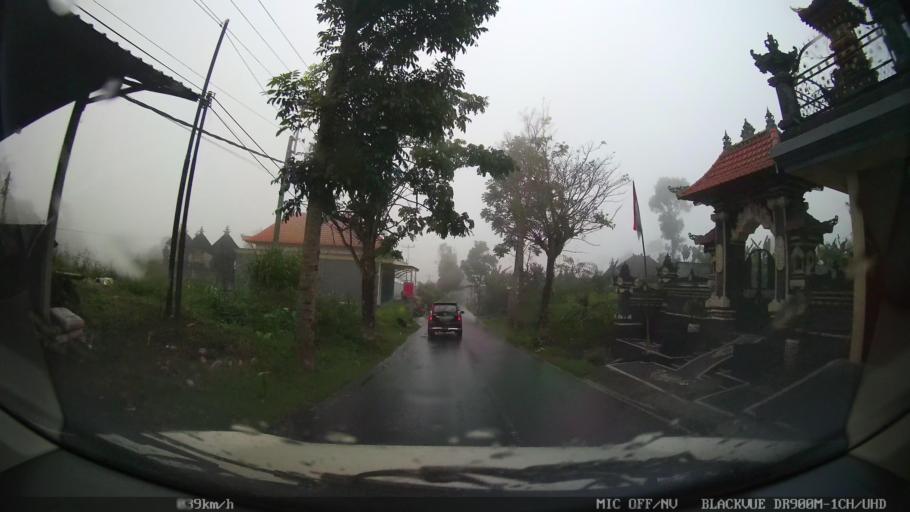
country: ID
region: Bali
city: Banjar Taro Kelod
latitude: -8.3176
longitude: 115.2991
